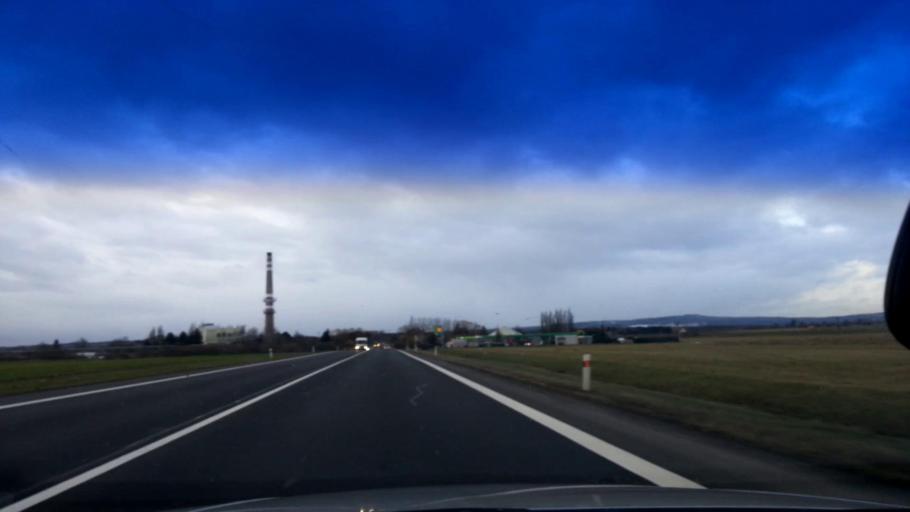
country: CZ
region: Karlovarsky
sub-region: Okres Cheb
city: Frantiskovy Lazne
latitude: 50.1255
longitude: 12.3614
